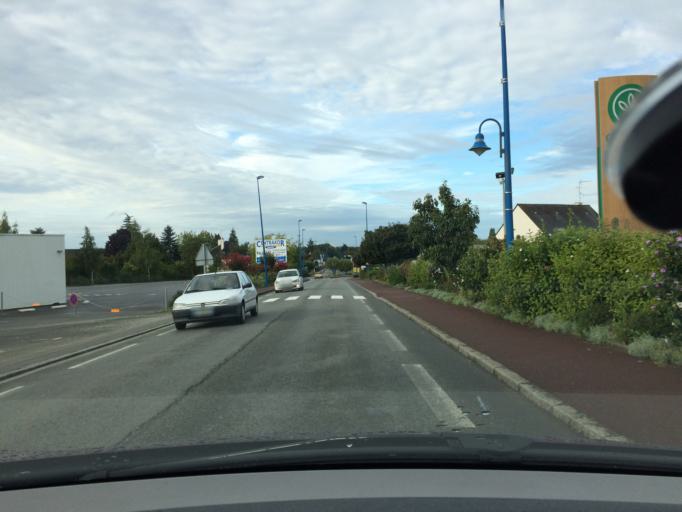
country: FR
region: Brittany
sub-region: Departement d'Ille-et-Vilaine
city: Janze
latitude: 47.9557
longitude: -1.5016
